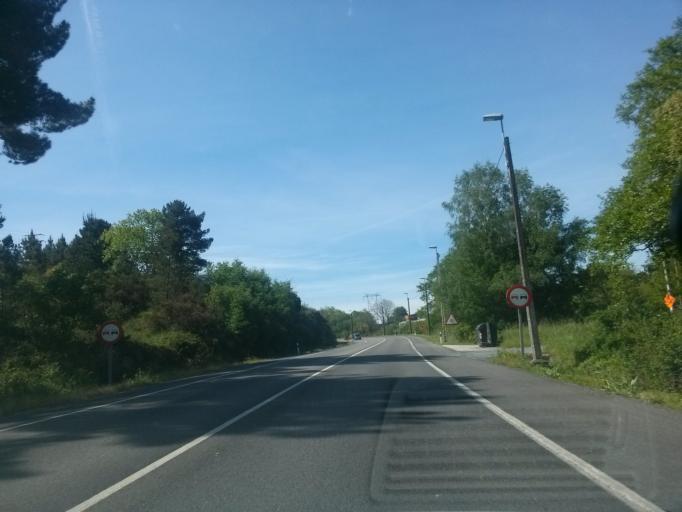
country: ES
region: Galicia
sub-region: Provincia de Lugo
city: Lugo
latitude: 42.9914
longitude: -7.5887
